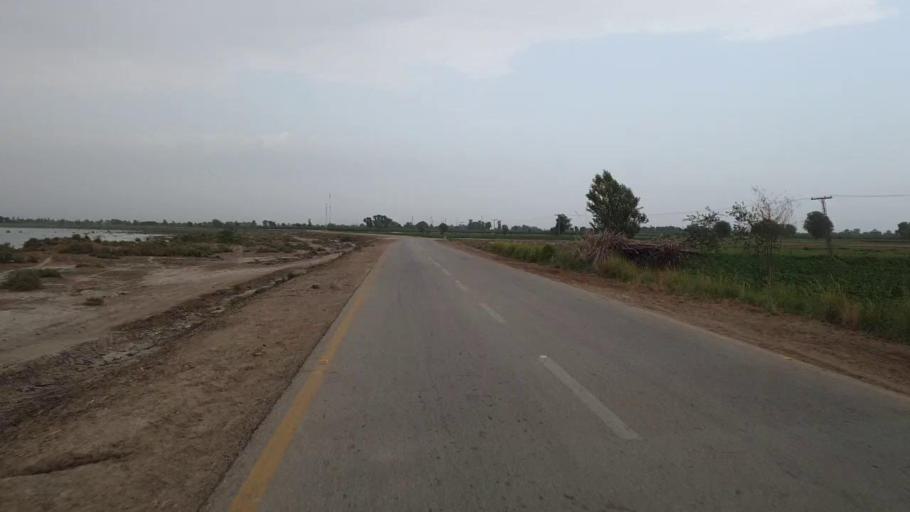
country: PK
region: Sindh
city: Bandhi
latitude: 26.5782
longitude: 68.2755
